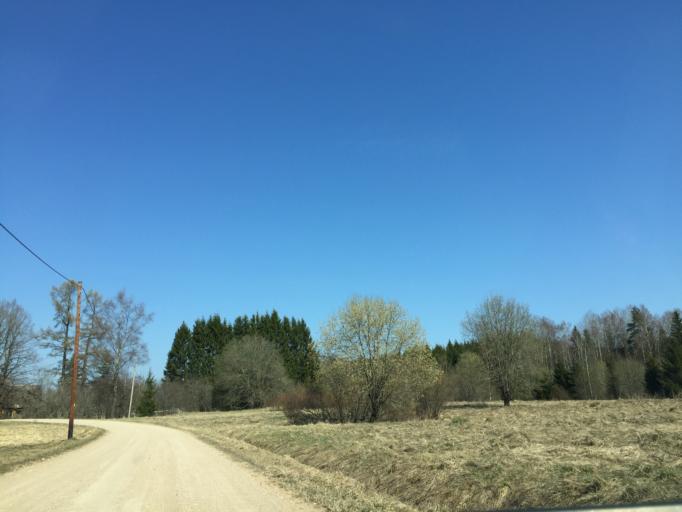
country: EE
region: Tartu
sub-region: Alatskivi vald
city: Kallaste
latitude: 58.5431
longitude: 26.9442
